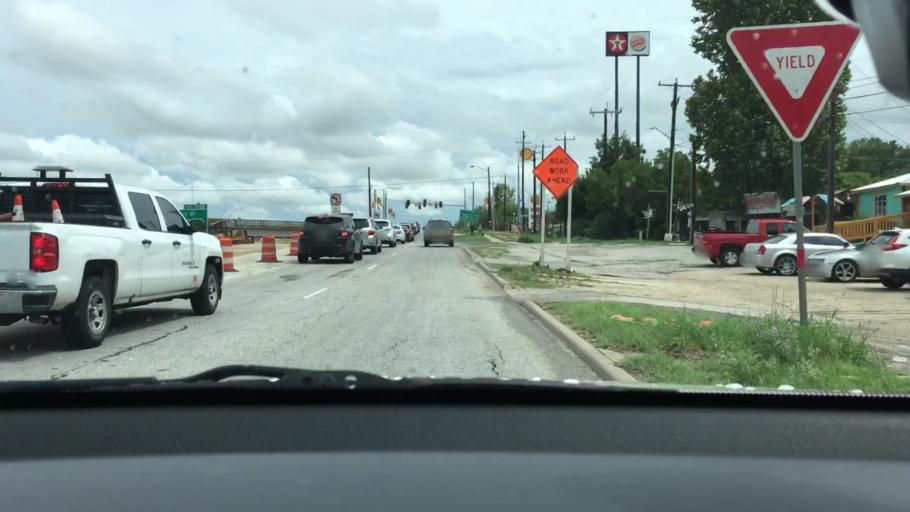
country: US
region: Texas
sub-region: Bexar County
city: San Antonio
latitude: 29.4379
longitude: -98.4628
